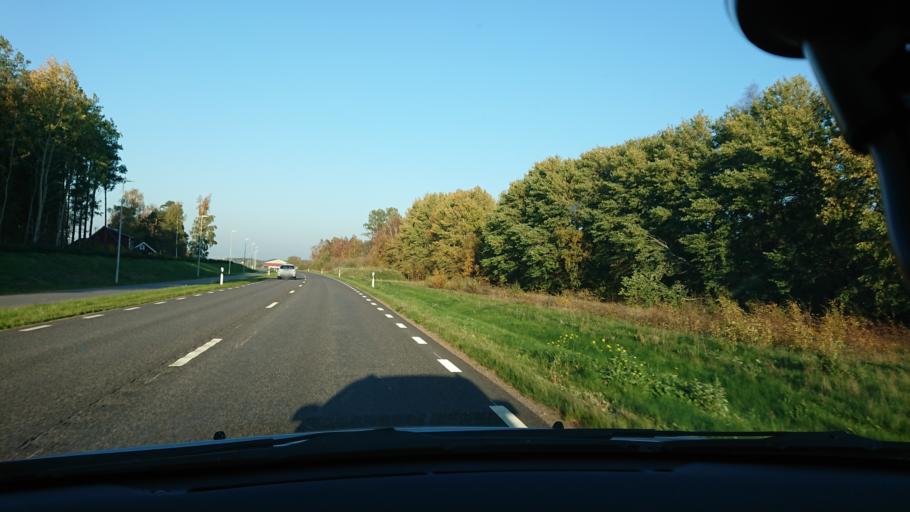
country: SE
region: Skane
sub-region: Bastads Kommun
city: Bastad
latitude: 56.4363
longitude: 12.9157
